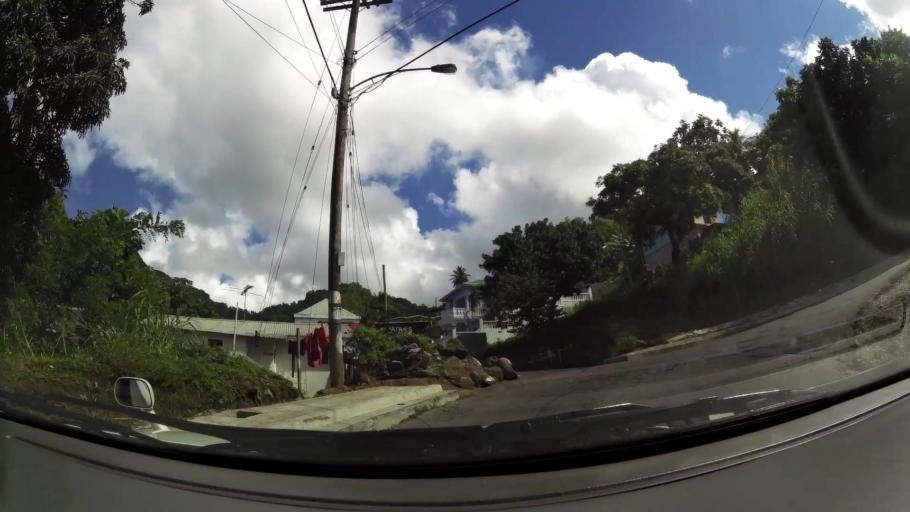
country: VC
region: Saint George
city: Kingstown Park
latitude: 13.1752
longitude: -61.2356
